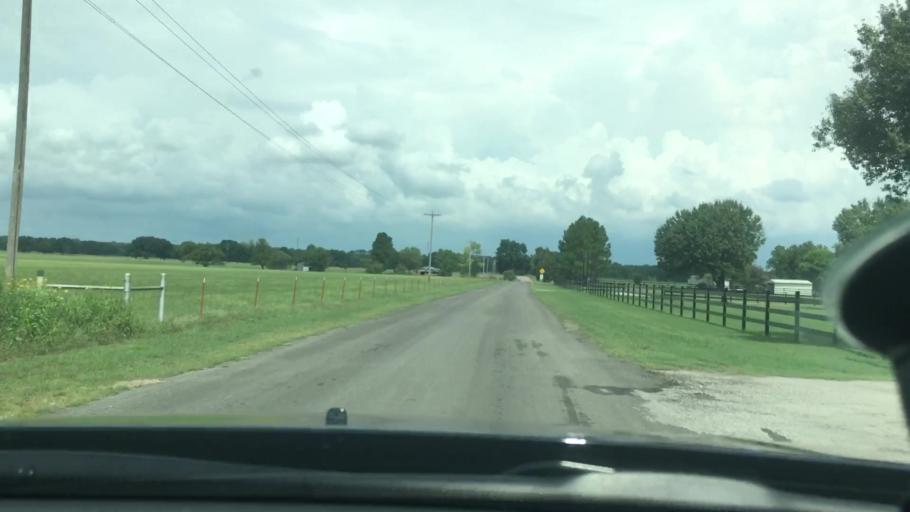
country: US
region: Oklahoma
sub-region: Carter County
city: Dickson
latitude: 34.2316
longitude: -96.9157
